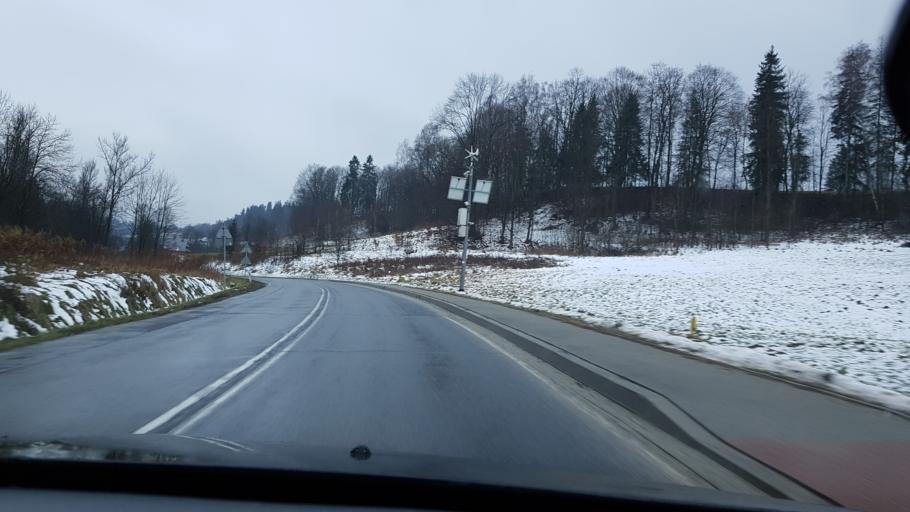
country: PL
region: Lesser Poland Voivodeship
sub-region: Powiat nowotarski
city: Raba Wyzna
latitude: 49.5365
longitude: 19.8880
